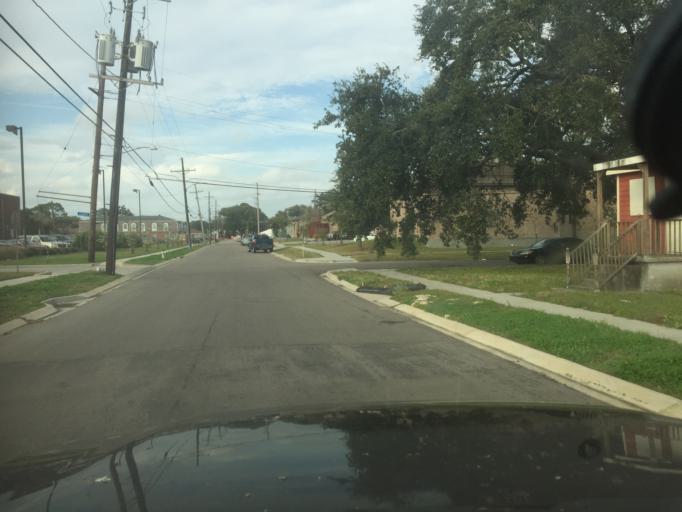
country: US
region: Louisiana
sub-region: Orleans Parish
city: New Orleans
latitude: 29.9973
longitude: -90.0819
